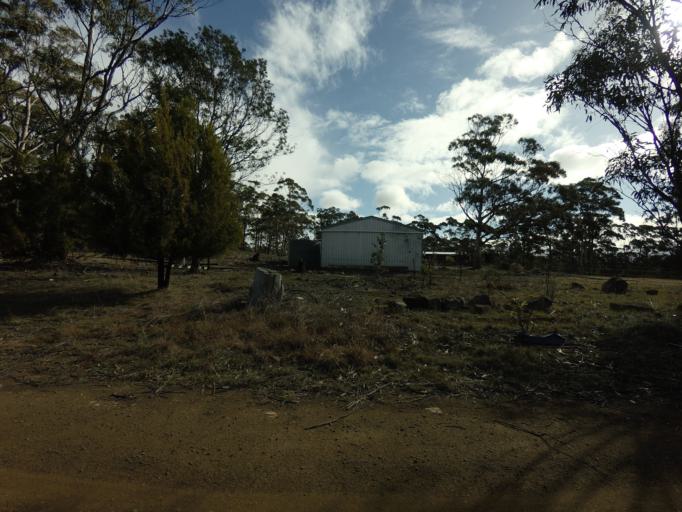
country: AU
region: Tasmania
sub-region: Sorell
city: Sorell
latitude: -42.3294
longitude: 147.9677
